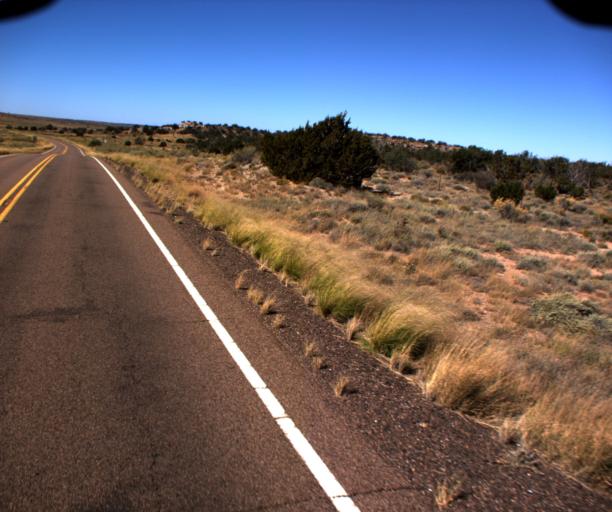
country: US
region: Arizona
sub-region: Navajo County
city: Taylor
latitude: 34.5094
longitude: -110.1759
